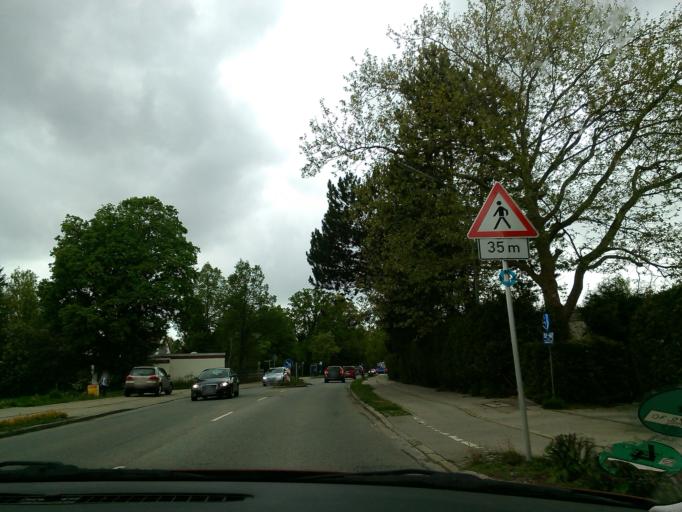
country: DE
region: Bavaria
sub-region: Upper Bavaria
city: Grafelfing
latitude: 48.1256
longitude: 11.4397
